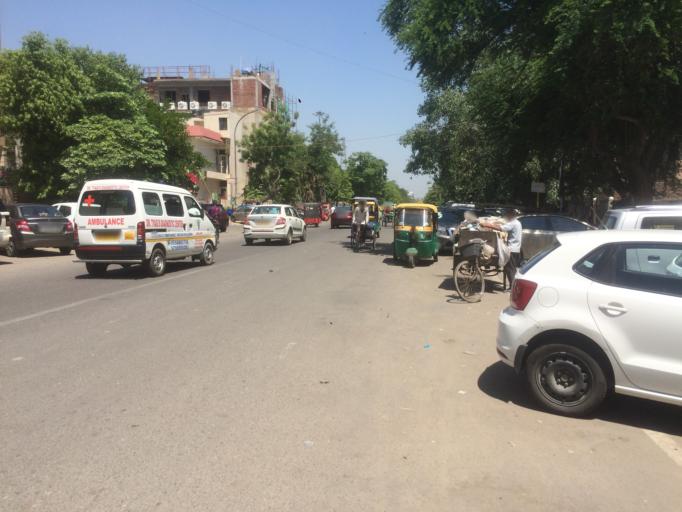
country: IN
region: Uttar Pradesh
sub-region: Gautam Buddha Nagar
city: Noida
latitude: 28.5769
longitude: 77.3328
